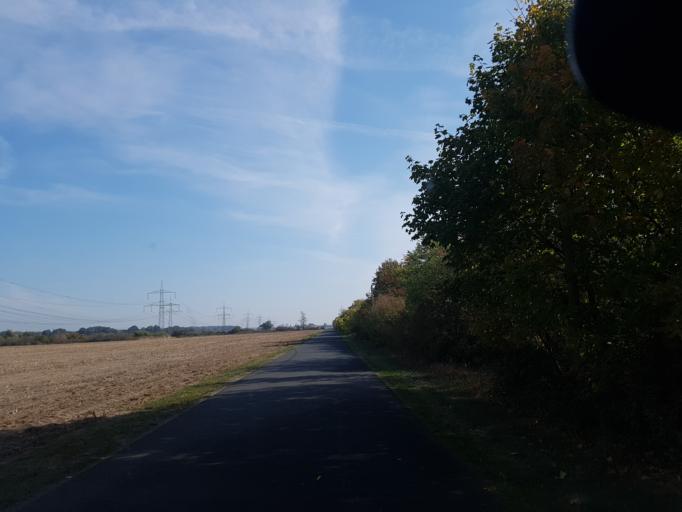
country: DE
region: Brandenburg
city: Ihlow
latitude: 51.8359
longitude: 13.3164
